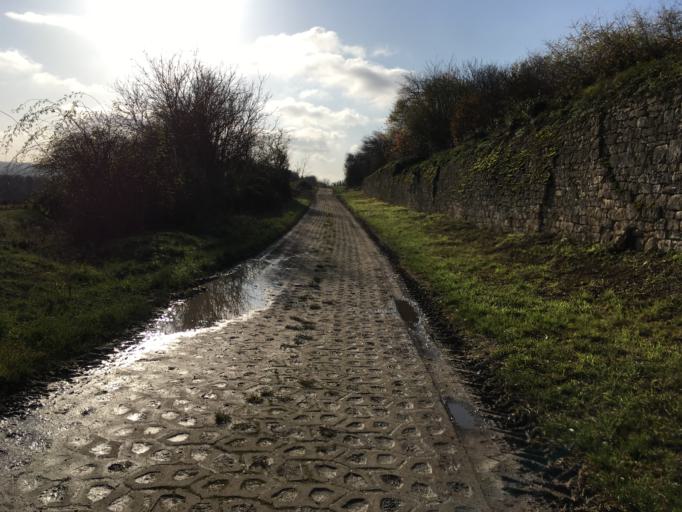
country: DE
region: Rheinland-Pfalz
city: Bodenheim
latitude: 49.9517
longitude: 8.3044
